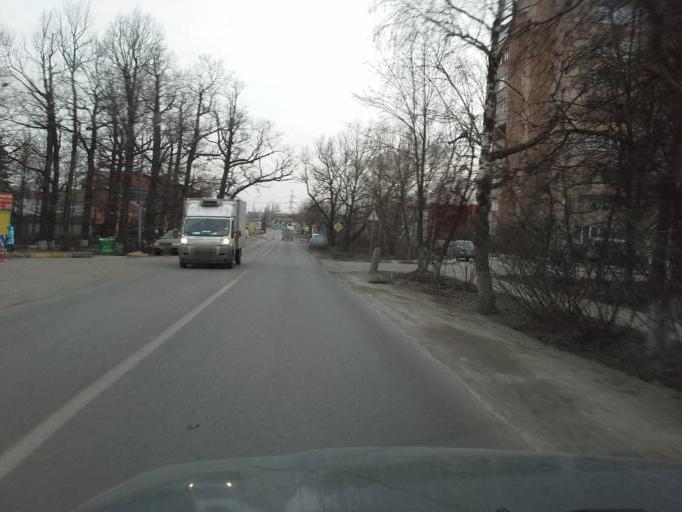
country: RU
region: Moskovskaya
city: Lesnoy Gorodok
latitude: 55.6595
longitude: 37.2123
